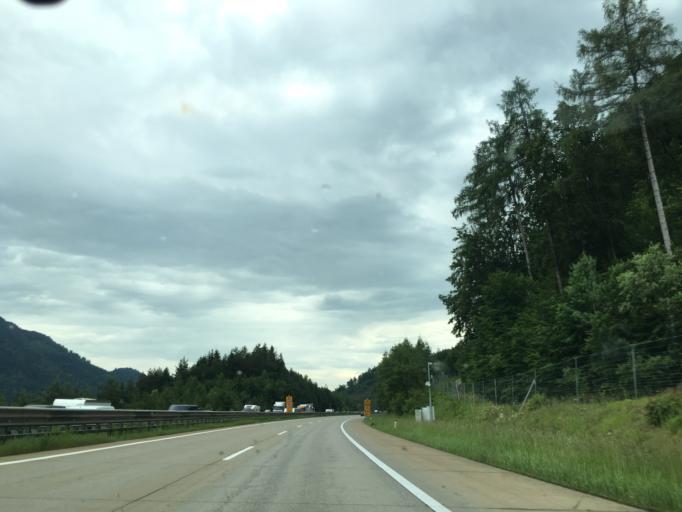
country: AT
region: Carinthia
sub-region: Villach Stadt
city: Villach
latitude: 46.6470
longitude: 13.7734
